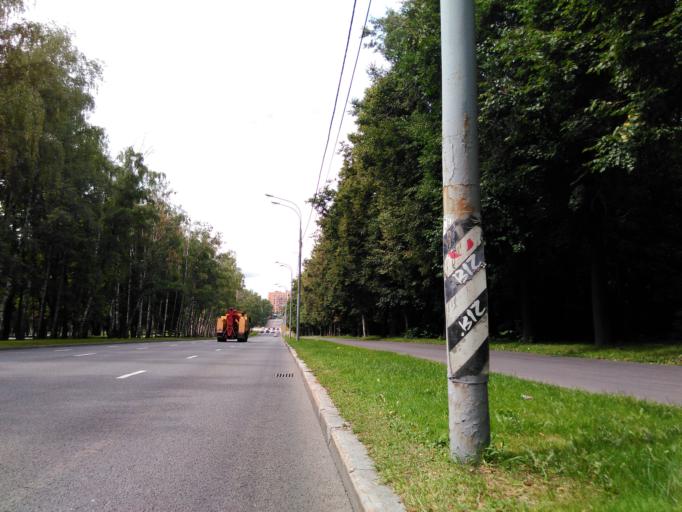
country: RU
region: Moscow
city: Vorob'yovo
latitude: 55.7093
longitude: 37.5324
